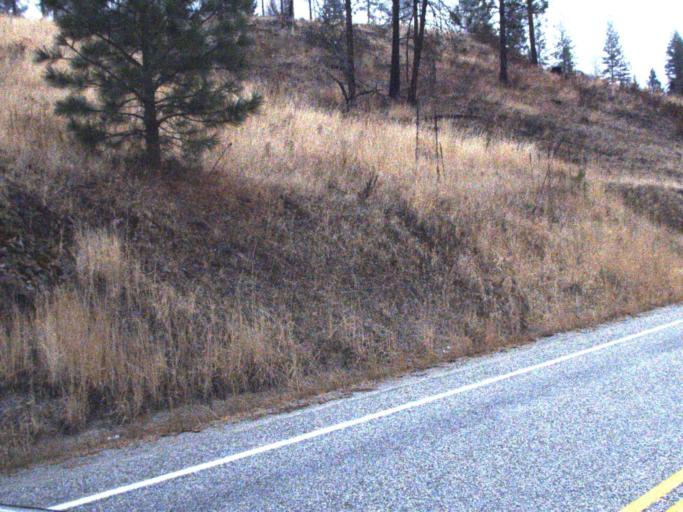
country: US
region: Washington
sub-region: Stevens County
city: Kettle Falls
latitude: 48.7531
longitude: -118.1346
